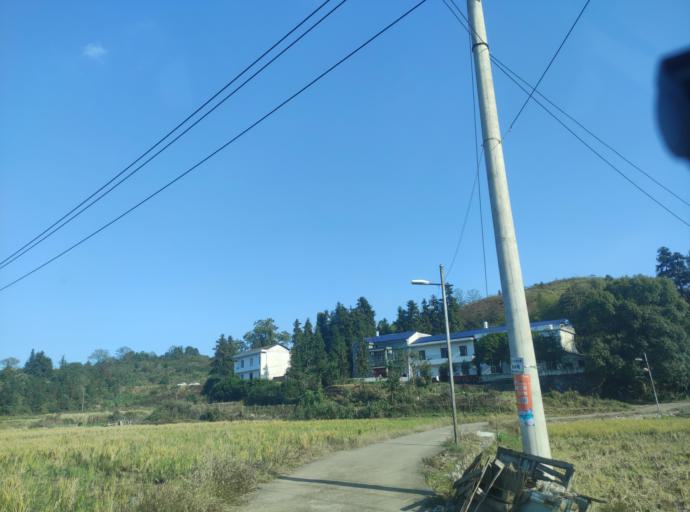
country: CN
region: Jiangxi Sheng
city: Xiangdong
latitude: 27.6549
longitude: 113.6637
